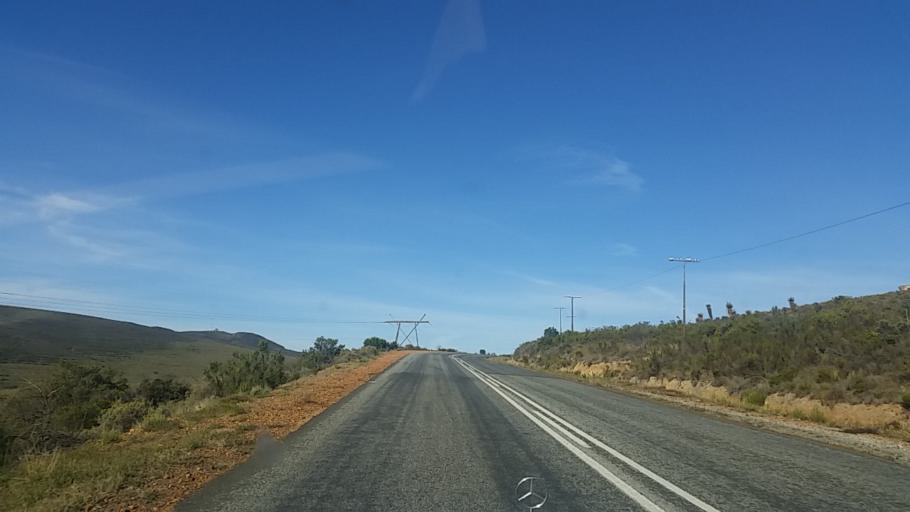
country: ZA
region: Western Cape
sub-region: Eden District Municipality
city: Knysna
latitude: -33.7425
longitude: 23.0232
